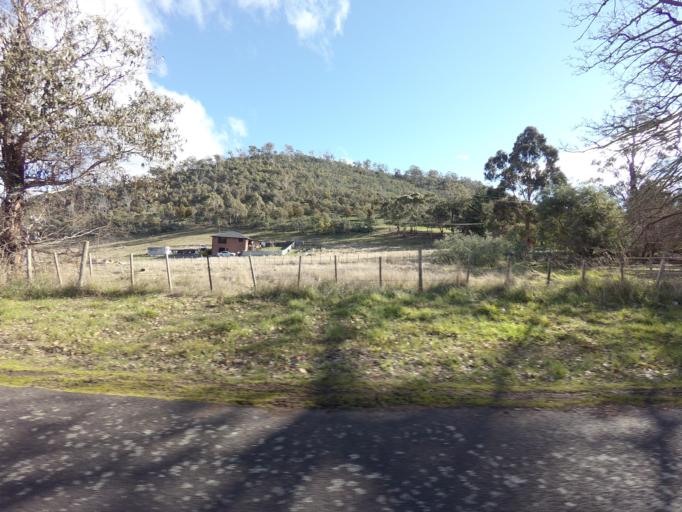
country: AU
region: Tasmania
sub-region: Derwent Valley
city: New Norfolk
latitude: -42.7497
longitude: 147.0462
